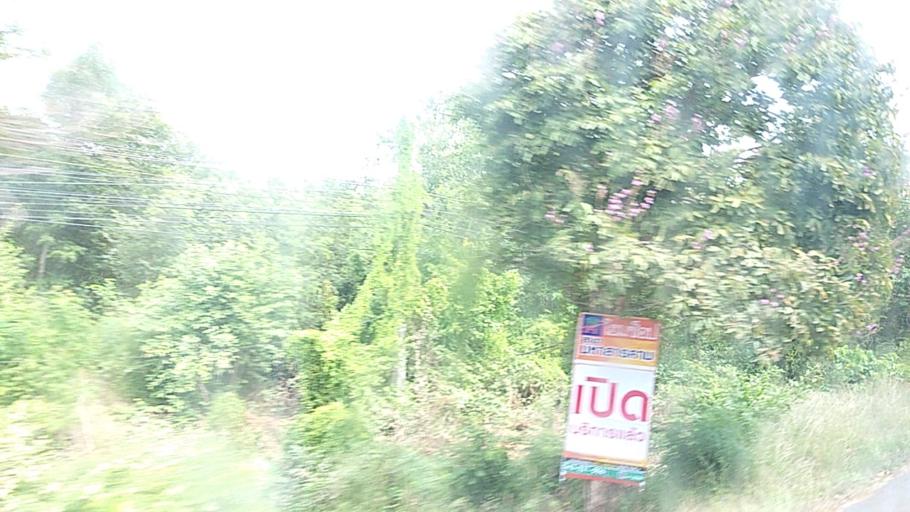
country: TH
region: Maha Sarakham
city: Maha Sarakham
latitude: 16.1613
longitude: 103.3512
